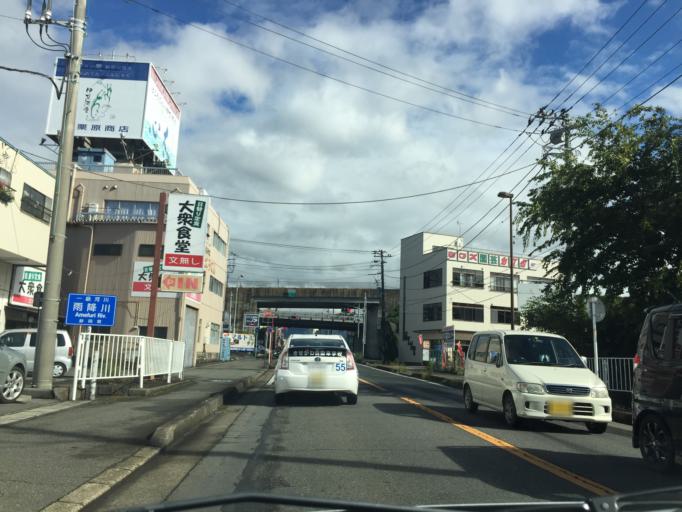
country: JP
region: Shizuoka
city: Mishima
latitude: 35.1096
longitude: 138.8928
